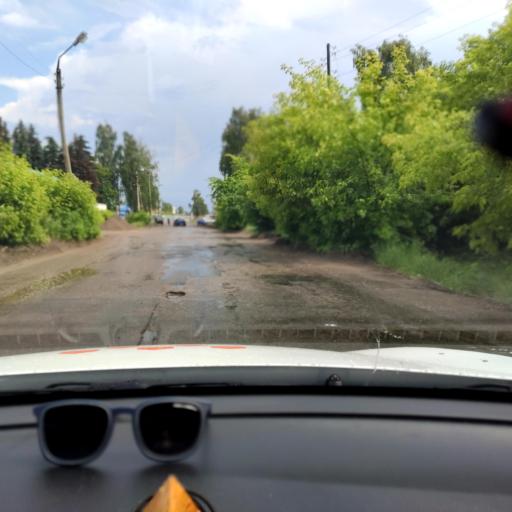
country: RU
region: Tatarstan
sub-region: Zelenodol'skiy Rayon
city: Vasil'yevo
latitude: 55.8369
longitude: 48.6808
